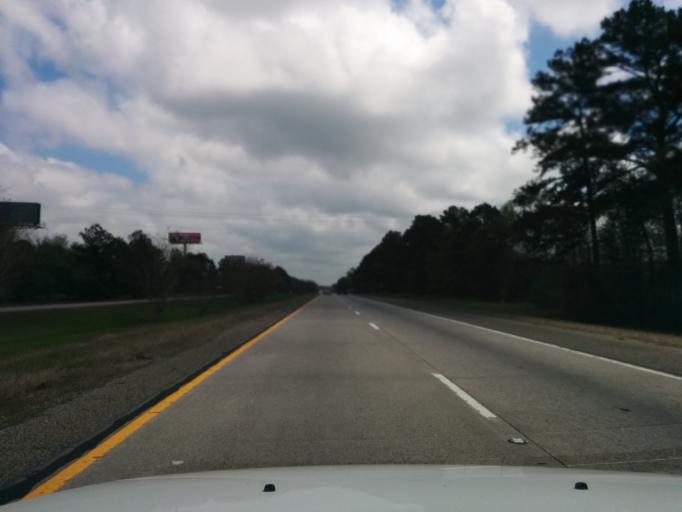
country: US
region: Georgia
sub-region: Bryan County
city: Pembroke
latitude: 32.2175
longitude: -81.5309
